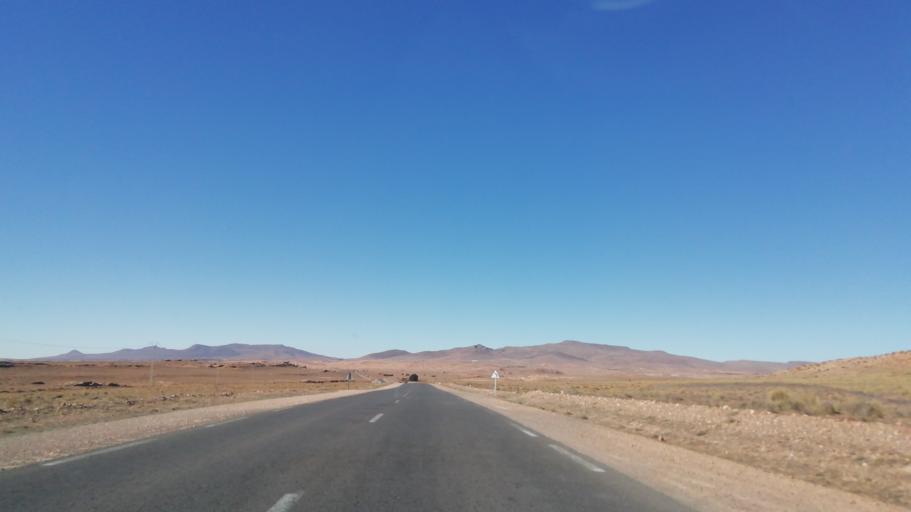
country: DZ
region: El Bayadh
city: El Bayadh
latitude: 33.6121
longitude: 1.2248
